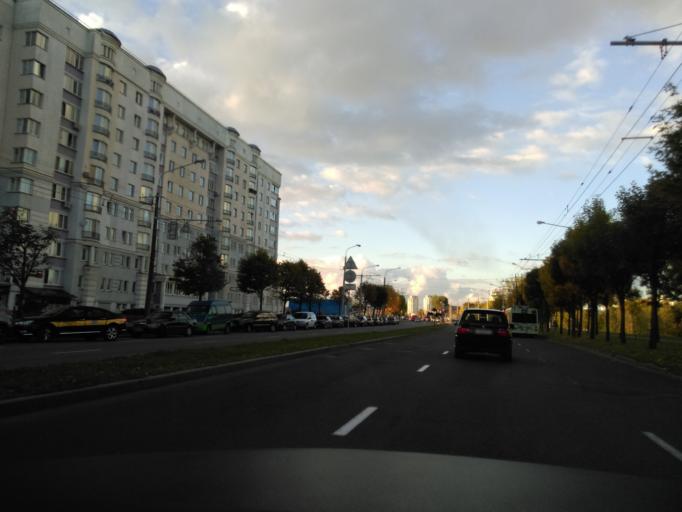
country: BY
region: Minsk
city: Minsk
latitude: 53.9250
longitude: 27.6392
